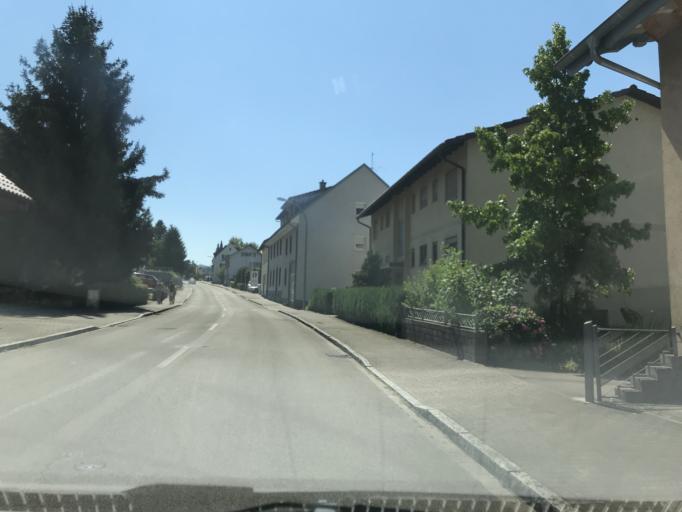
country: DE
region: Baden-Wuerttemberg
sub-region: Freiburg Region
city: Wehr
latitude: 47.6325
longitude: 7.9008
